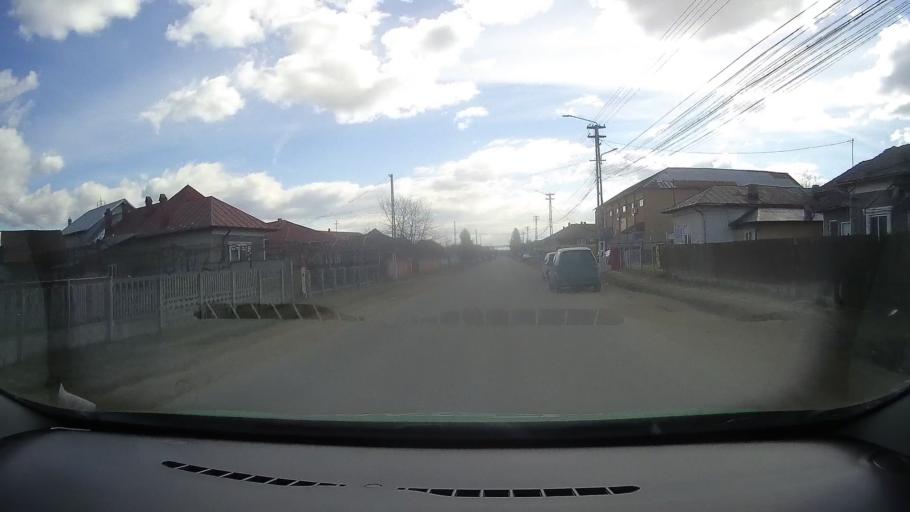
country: RO
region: Dambovita
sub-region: Comuna Doicesti
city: Doicesti
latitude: 44.9838
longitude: 25.3873
